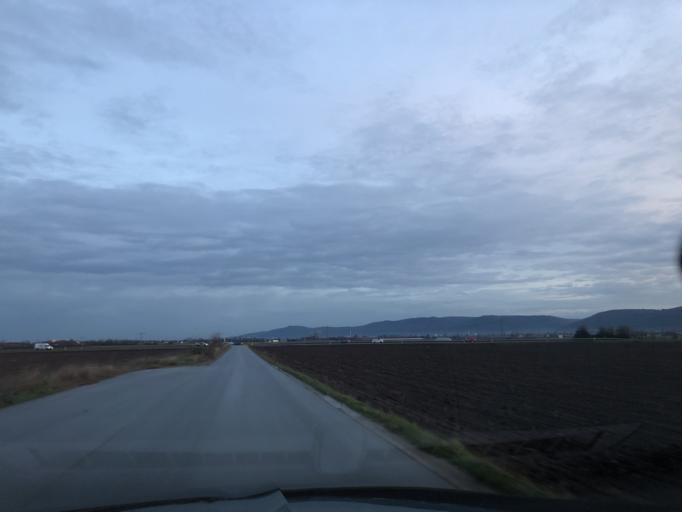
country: DE
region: Baden-Wuerttemberg
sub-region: Karlsruhe Region
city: Sandhausen
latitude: 49.3609
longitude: 8.6366
